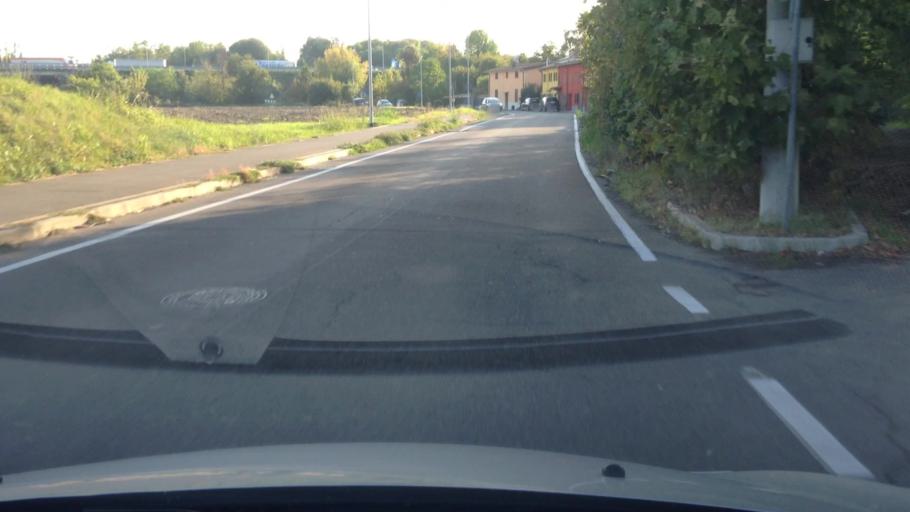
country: IT
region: Emilia-Romagna
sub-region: Provincia di Modena
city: Baggiovara
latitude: 44.6195
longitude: 10.8898
